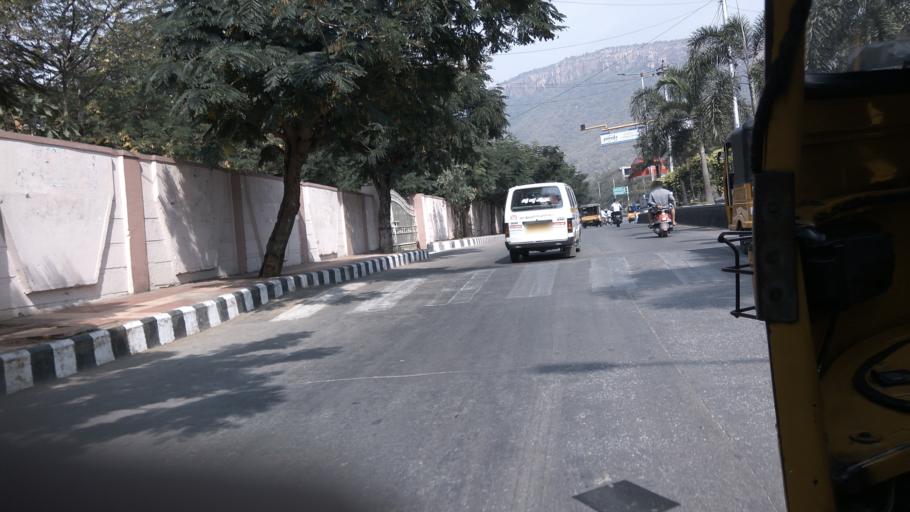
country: IN
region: Andhra Pradesh
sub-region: Chittoor
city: Tirupati
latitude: 13.6415
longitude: 79.4095
